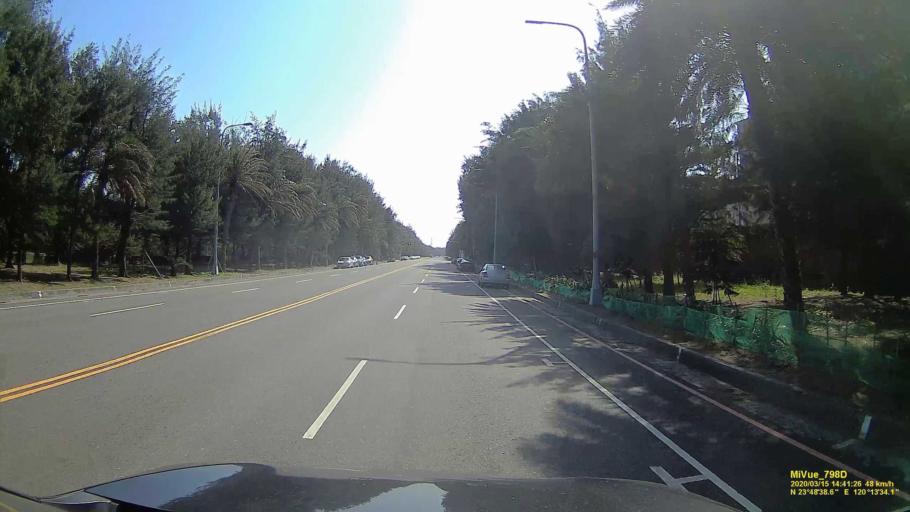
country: TW
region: Taiwan
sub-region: Yunlin
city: Douliu
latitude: 23.8106
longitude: 120.2260
